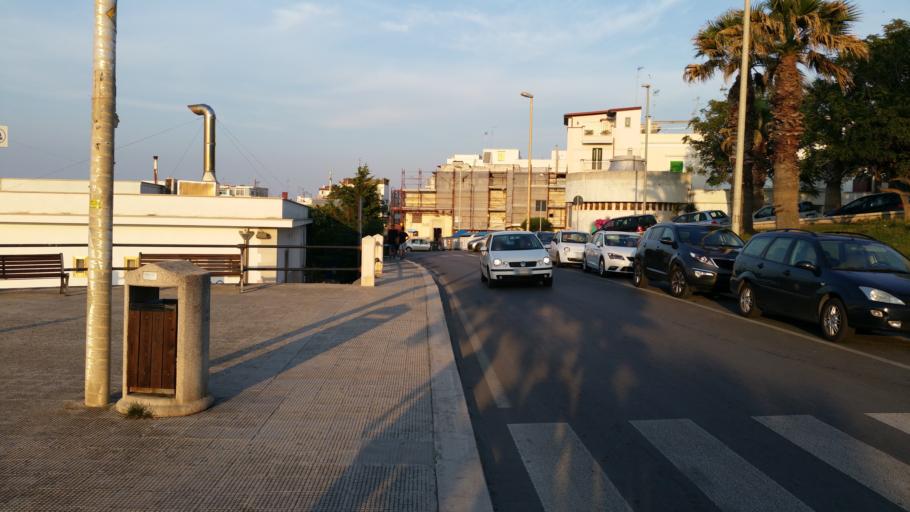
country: IT
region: Apulia
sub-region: Provincia di Bari
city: Parco Scizzo-Parchitello
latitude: 41.0879
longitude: 16.9993
